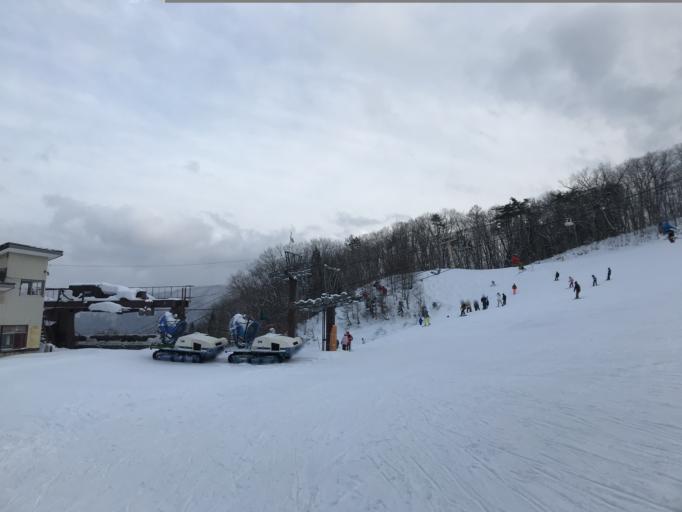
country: JP
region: Nagano
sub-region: Kitaazumi Gun
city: Hakuba
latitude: 36.7028
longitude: 137.8349
